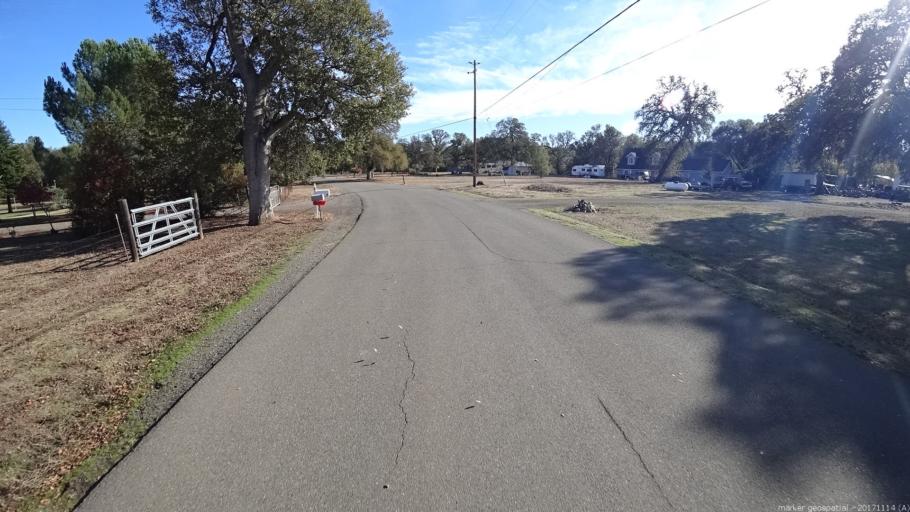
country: US
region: California
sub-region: Shasta County
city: Anderson
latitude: 40.3808
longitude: -122.4513
